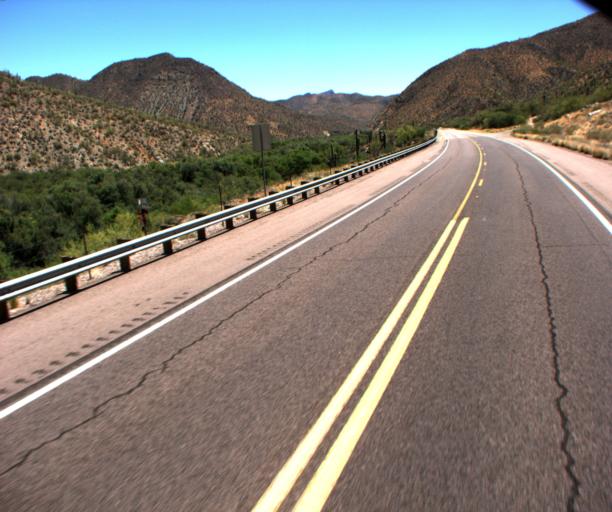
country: US
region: Arizona
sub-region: Pinal County
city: Kearny
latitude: 33.0673
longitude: -110.7261
